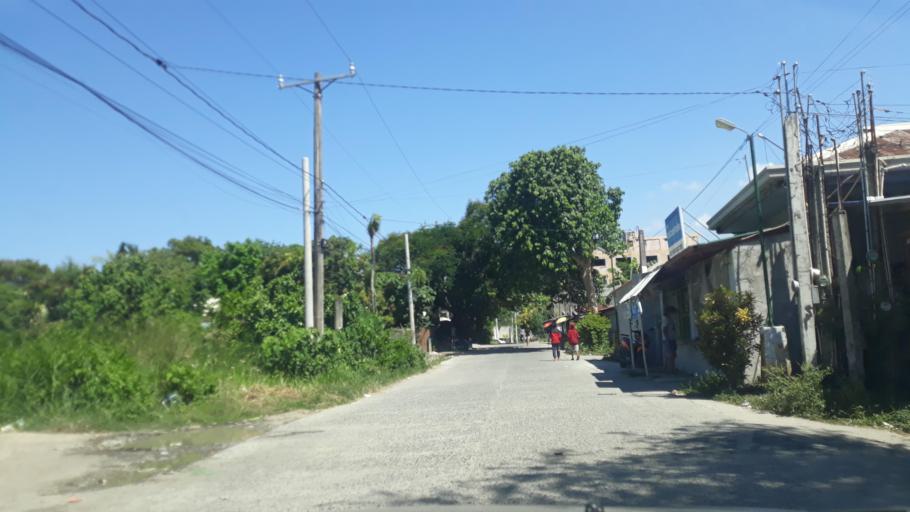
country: PH
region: Calabarzon
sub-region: Province of Cavite
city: Manggahan
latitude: 14.3001
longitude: 120.9163
